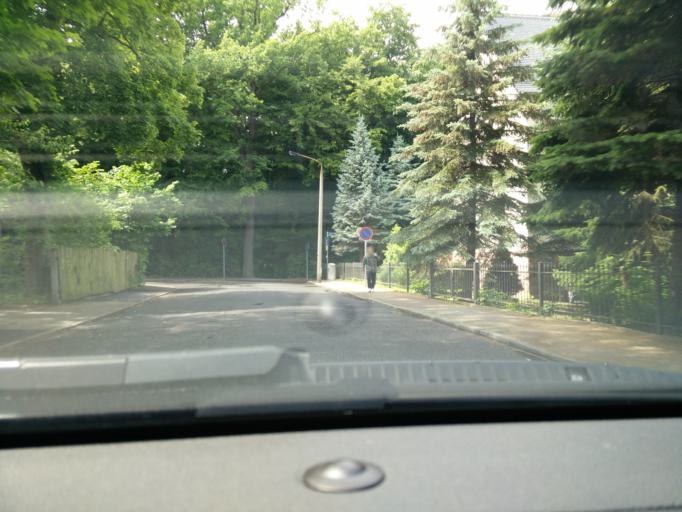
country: DE
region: Saxony
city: Bad Lausick
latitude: 51.1504
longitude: 12.6530
